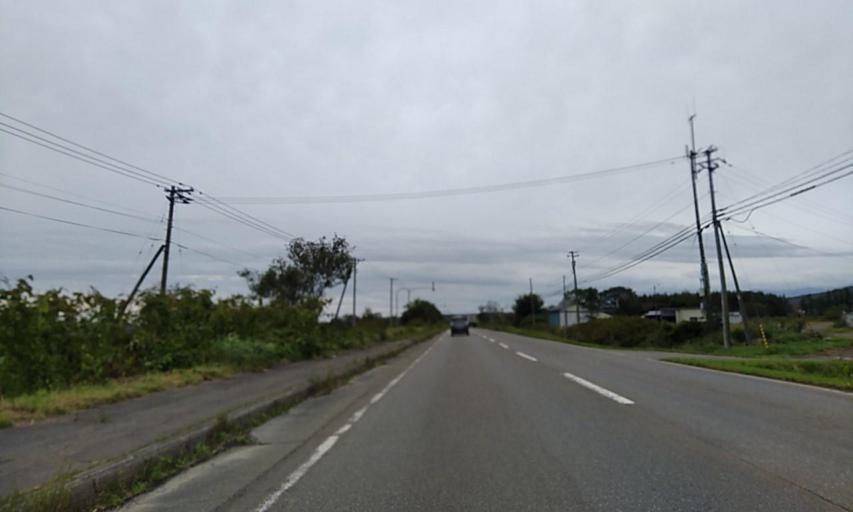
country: JP
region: Hokkaido
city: Obihiro
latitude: 42.4757
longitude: 143.2741
